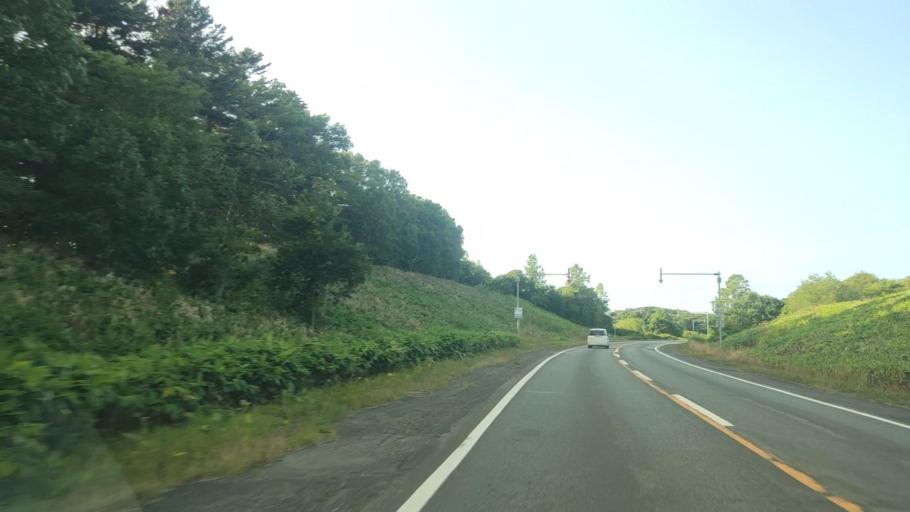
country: JP
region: Hokkaido
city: Makubetsu
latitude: 45.0667
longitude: 141.7481
